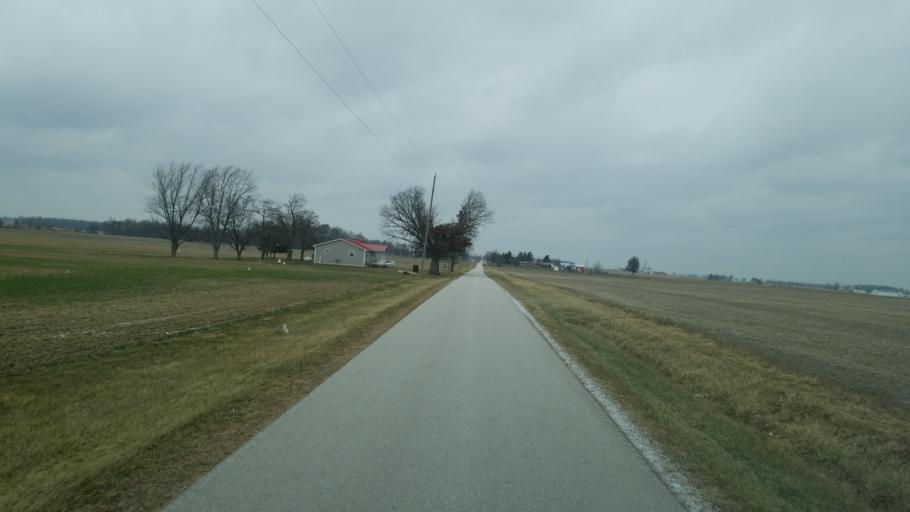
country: US
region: Ohio
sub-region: Hardin County
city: Forest
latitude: 40.7640
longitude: -83.4777
